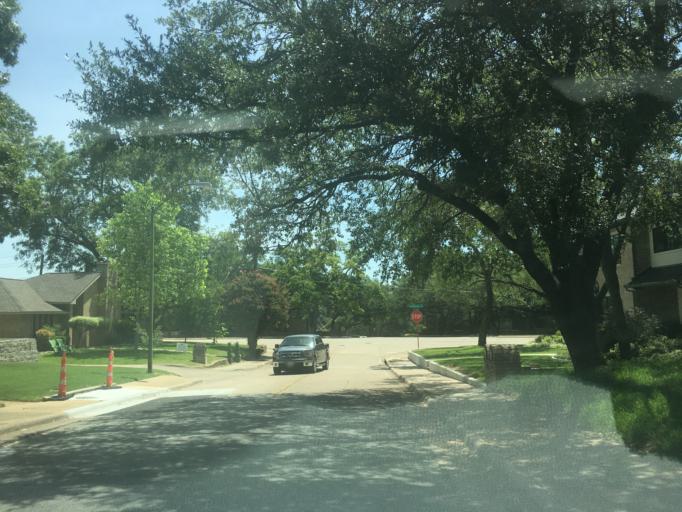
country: US
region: Texas
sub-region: Dallas County
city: Richardson
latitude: 32.8830
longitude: -96.7364
